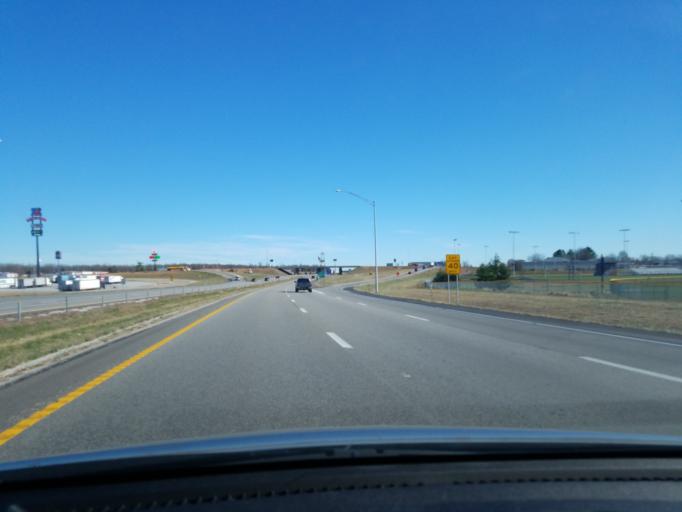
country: US
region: Missouri
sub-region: Greene County
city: Strafford
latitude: 37.2727
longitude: -93.1184
